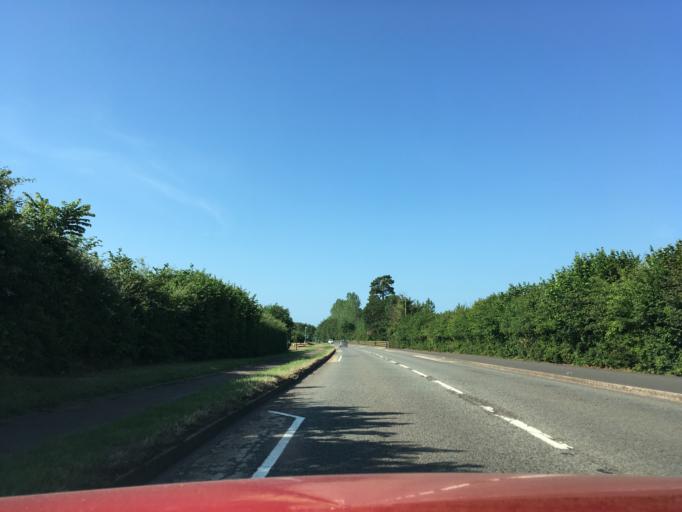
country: GB
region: England
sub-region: Gloucestershire
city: Lydney
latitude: 51.7212
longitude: -2.5413
